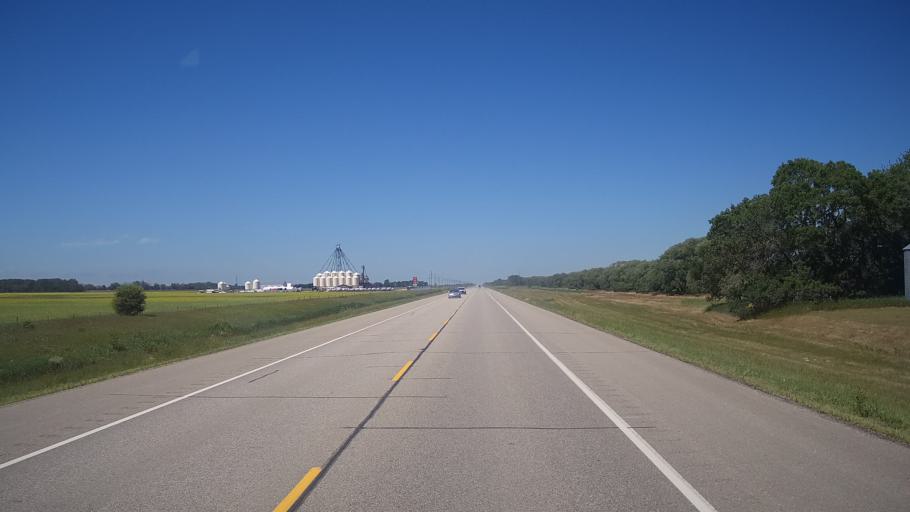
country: CA
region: Manitoba
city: Neepawa
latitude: 50.2257
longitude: -99.0332
